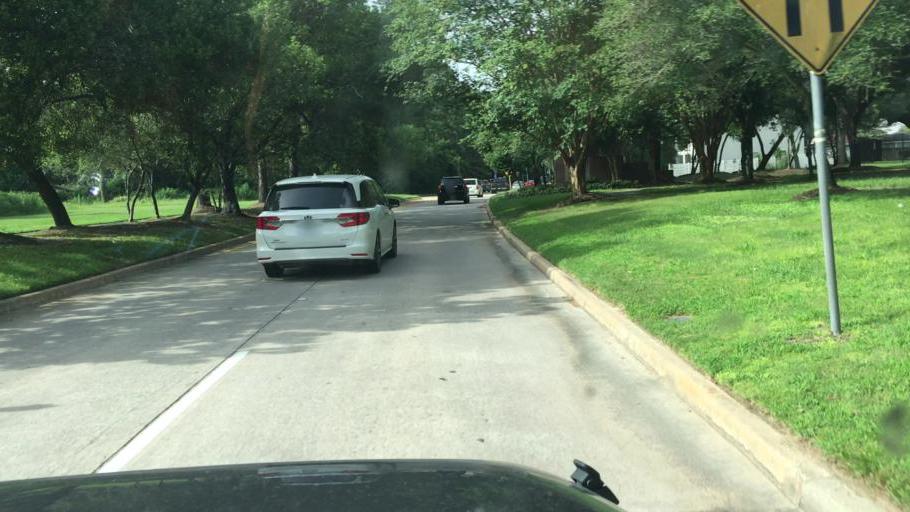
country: US
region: Texas
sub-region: Harris County
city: Atascocita
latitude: 30.0009
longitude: -95.1780
